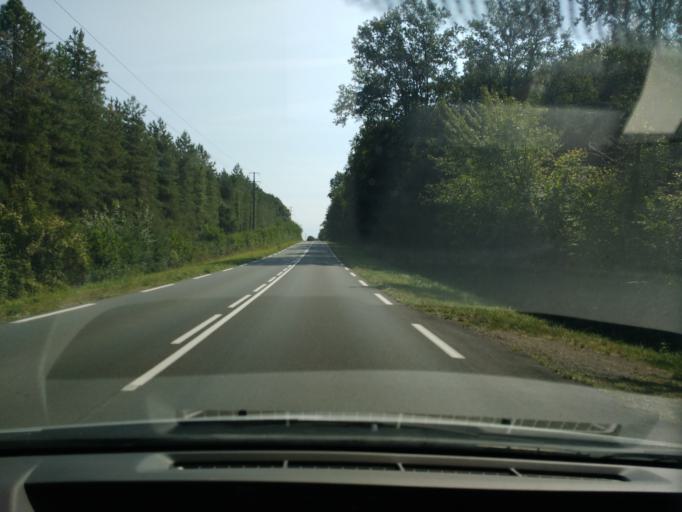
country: FR
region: Pays de la Loire
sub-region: Departement de Maine-et-Loire
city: Bauge-en-Anjou
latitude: 47.5328
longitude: -0.0619
